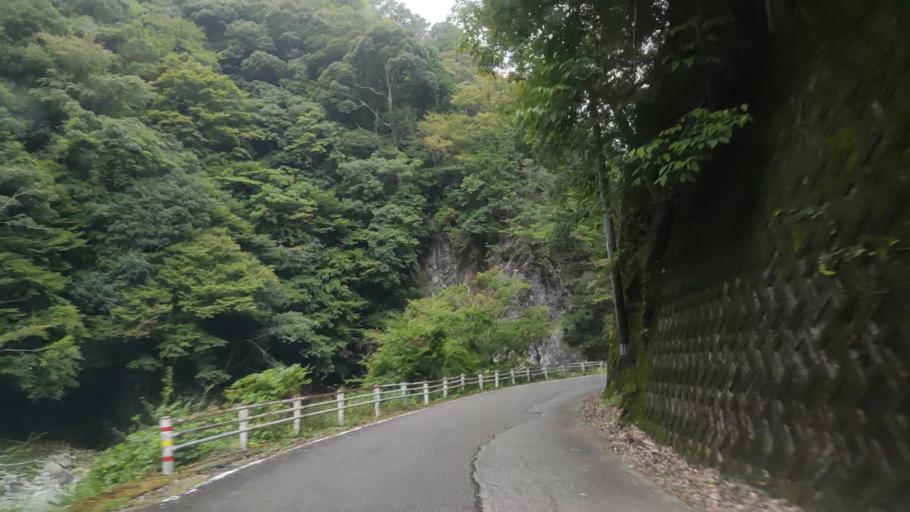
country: JP
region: Wakayama
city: Koya
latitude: 34.2640
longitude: 135.6453
